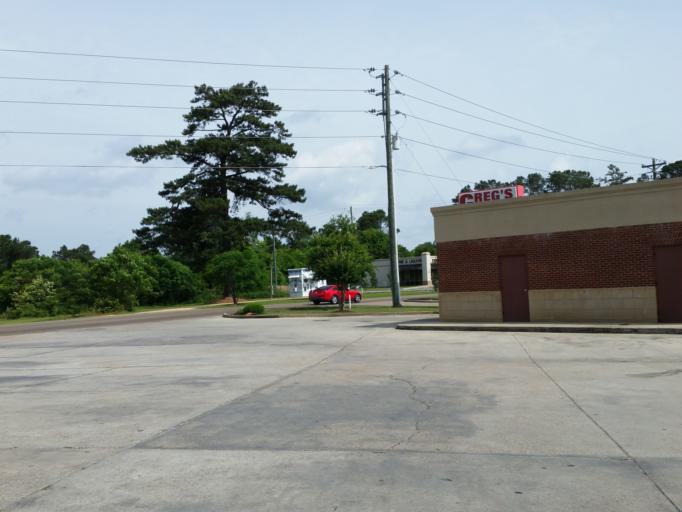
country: US
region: Mississippi
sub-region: Lamar County
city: West Hattiesburg
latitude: 31.3013
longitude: -89.3767
